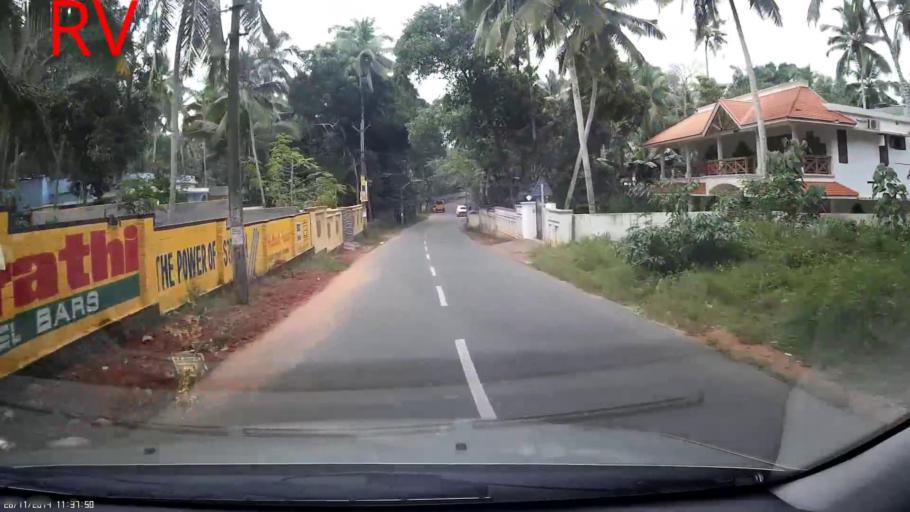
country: IN
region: Kerala
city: Kovalam
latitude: 8.3927
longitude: 77.0276
